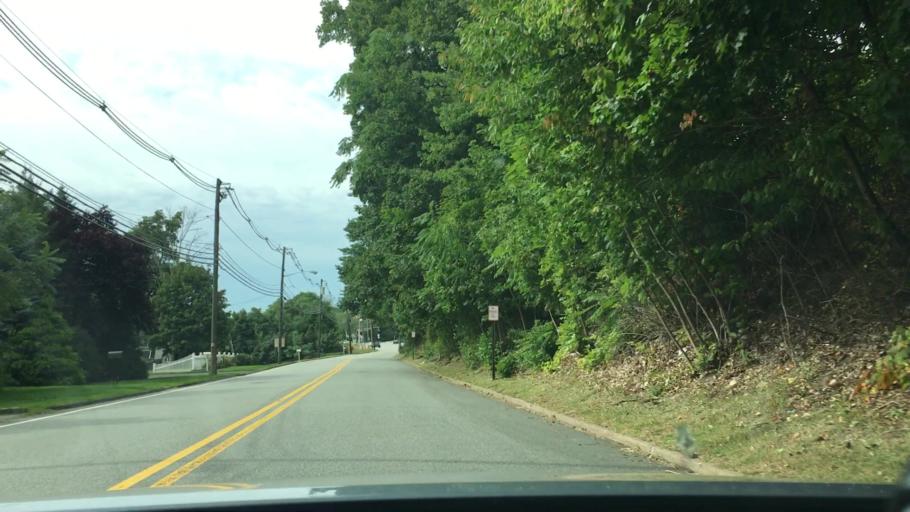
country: US
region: New Jersey
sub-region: Bergen County
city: Woodcliff Lake
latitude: 41.0105
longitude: -74.0699
